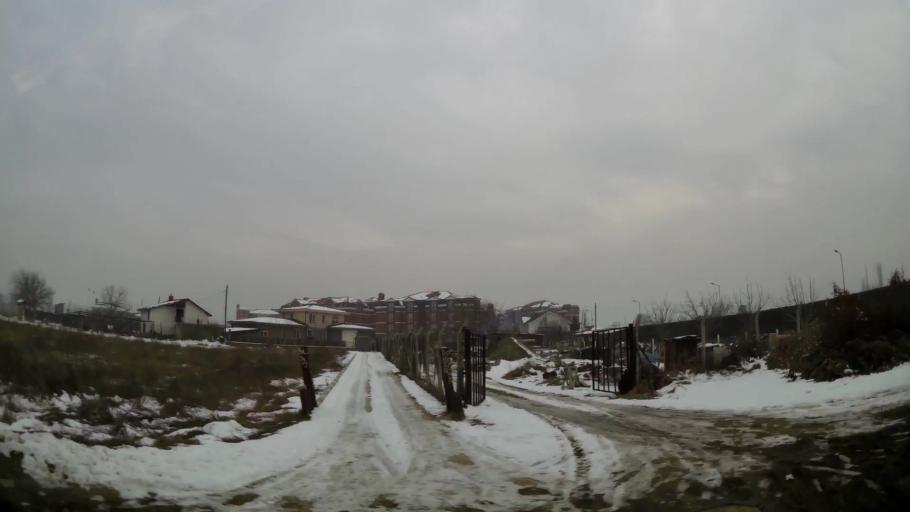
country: MK
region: Cucer-Sandevo
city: Chucher - Sandevo
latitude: 42.0510
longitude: 21.3649
